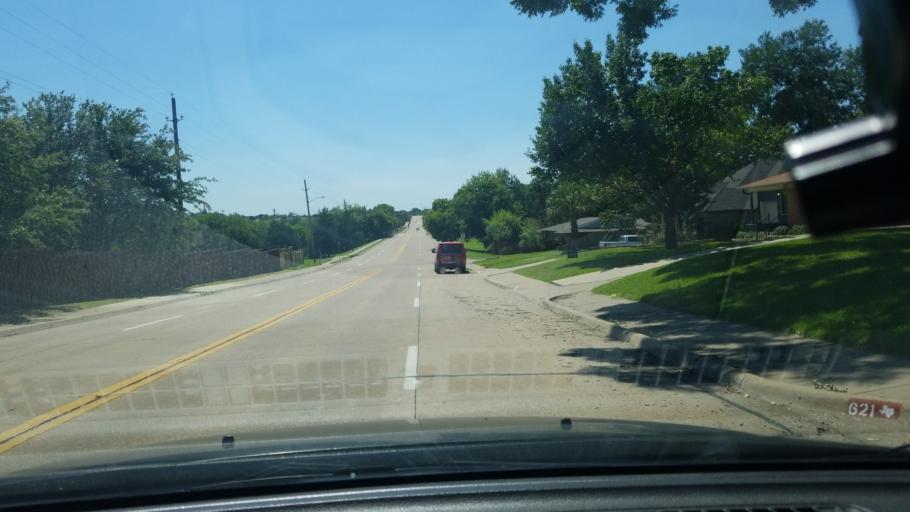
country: US
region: Texas
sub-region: Dallas County
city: Mesquite
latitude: 32.7560
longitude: -96.6063
